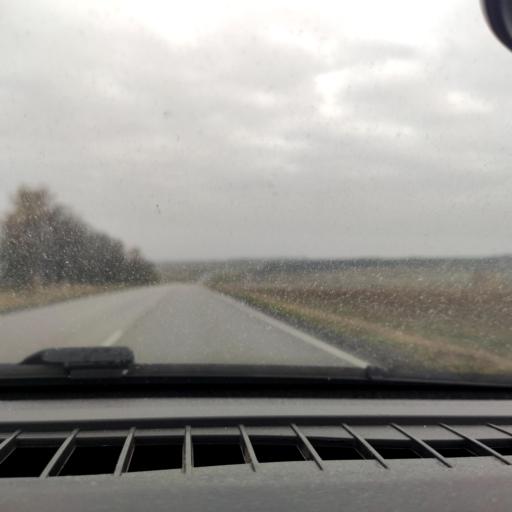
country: RU
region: Belgorod
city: Ilovka
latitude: 50.7644
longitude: 38.7457
